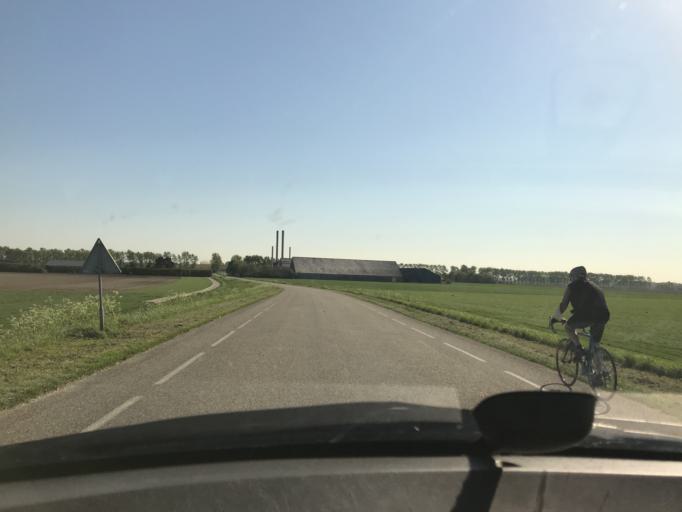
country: NL
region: Zeeland
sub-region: Gemeente Noord-Beveland
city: Kamperland
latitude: 51.5780
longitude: 3.8082
